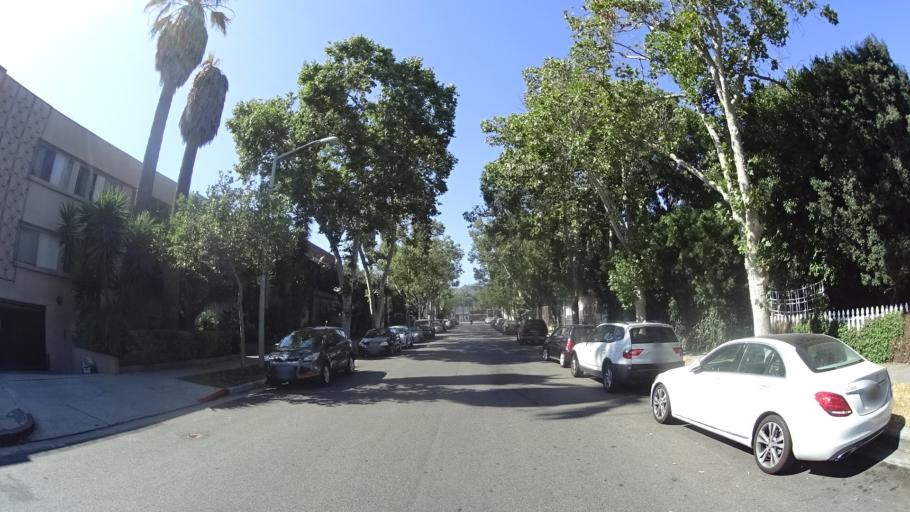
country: US
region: California
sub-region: Los Angeles County
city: West Hollywood
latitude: 34.0895
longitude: -118.3627
